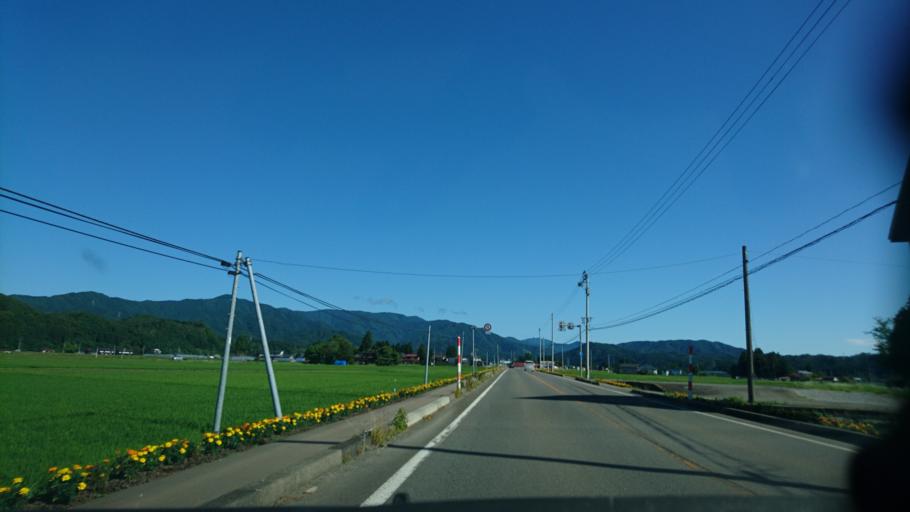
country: JP
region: Akita
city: Kakunodatemachi
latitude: 39.6426
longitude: 140.5711
